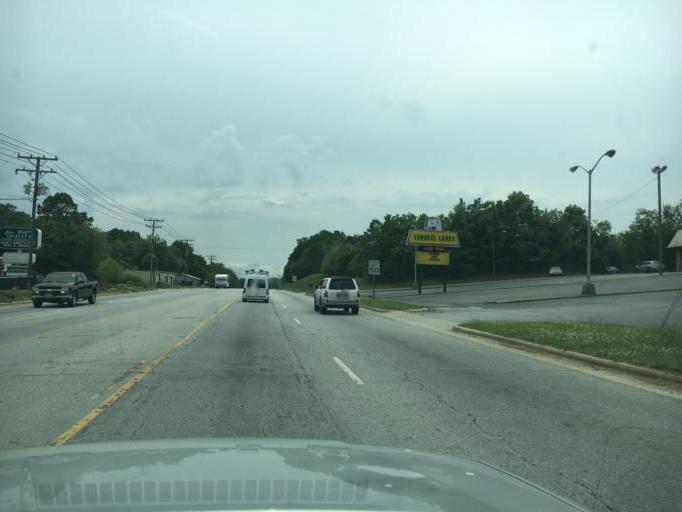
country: US
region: North Carolina
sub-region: Henderson County
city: Mountain Home
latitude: 35.3609
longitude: -82.4807
